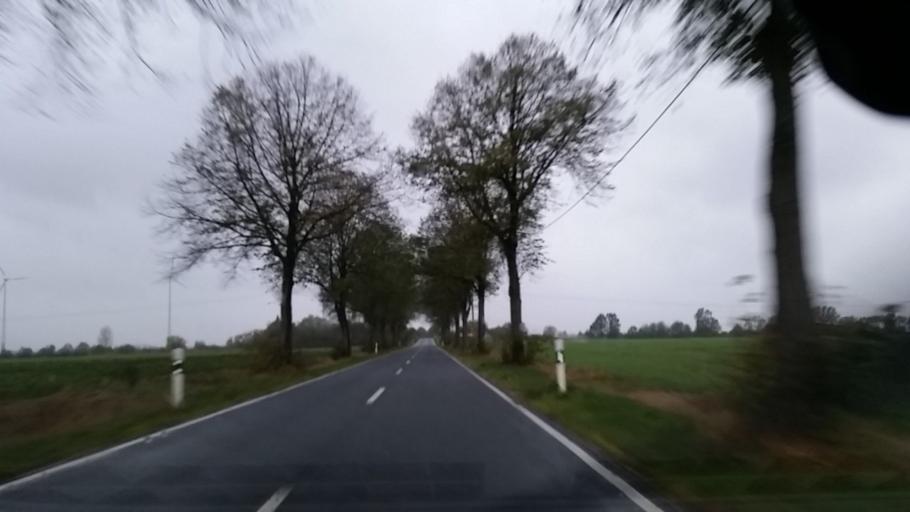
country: DE
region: Lower Saxony
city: Calberlah
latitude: 52.3999
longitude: 10.6804
